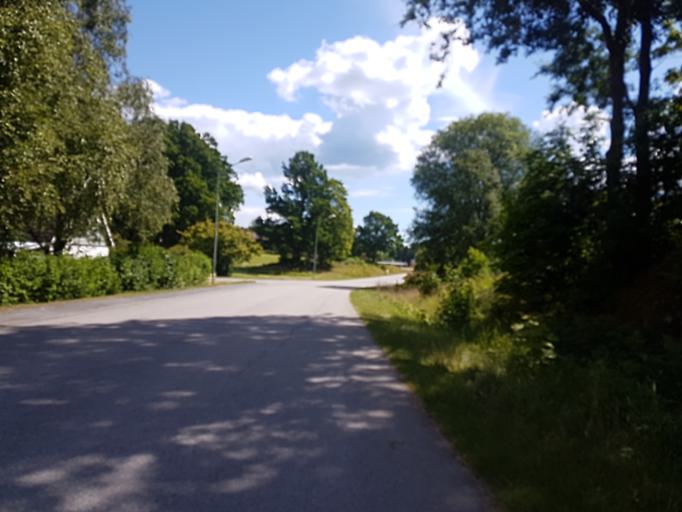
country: SE
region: Soedermanland
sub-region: Gnesta Kommun
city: Gnesta
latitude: 59.0349
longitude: 17.3265
